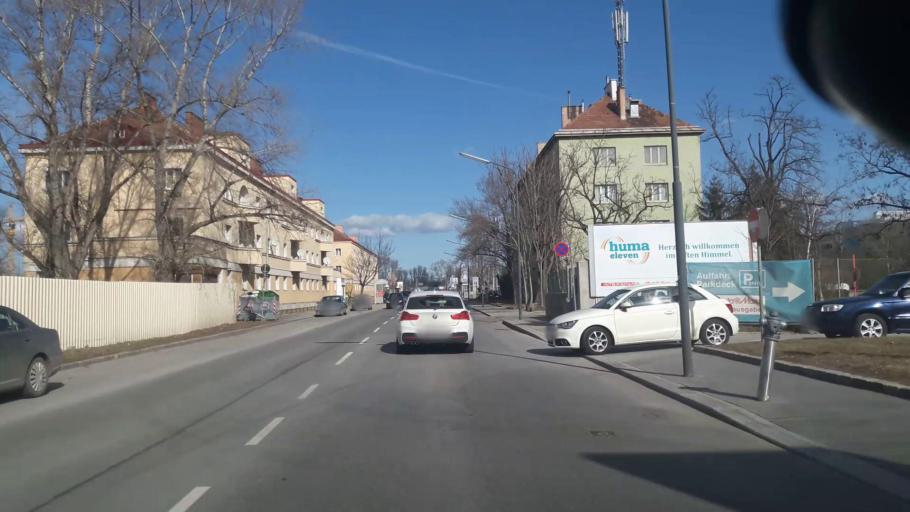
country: AT
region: Lower Austria
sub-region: Politischer Bezirk Wien-Umgebung
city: Schwechat
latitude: 48.1681
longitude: 16.4700
